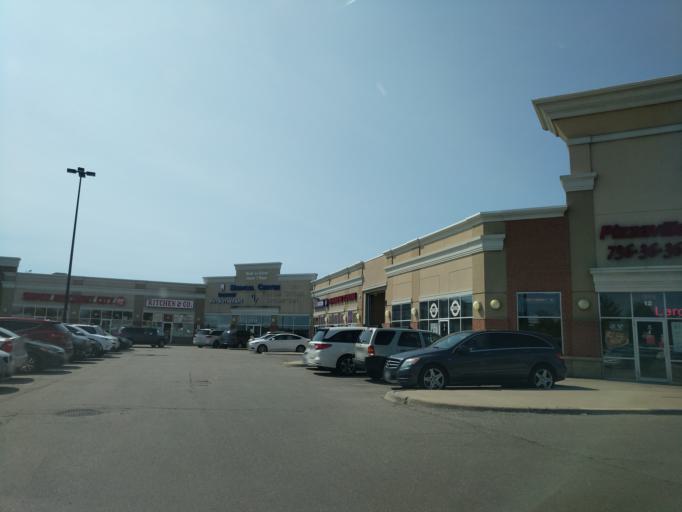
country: CA
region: Ontario
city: Markham
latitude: 43.8322
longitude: -79.2663
